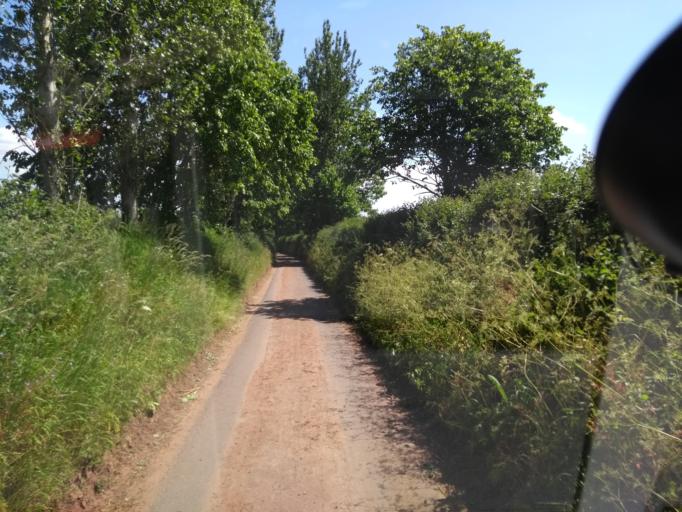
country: GB
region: England
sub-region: Somerset
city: North Petherton
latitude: 51.0653
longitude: -3.0096
